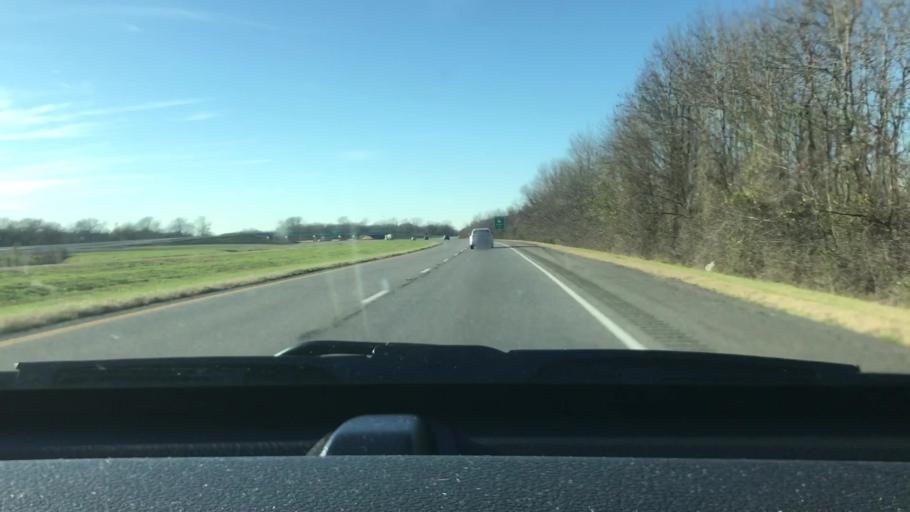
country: US
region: Louisiana
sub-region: Rapides Parish
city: Boyce
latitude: 31.3786
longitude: -92.6464
